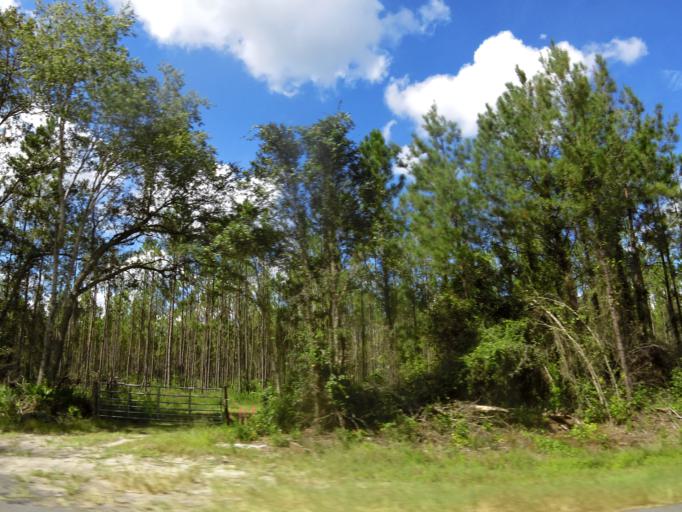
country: US
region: Florida
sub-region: Hamilton County
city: Jasper
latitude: 30.6315
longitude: -82.5969
